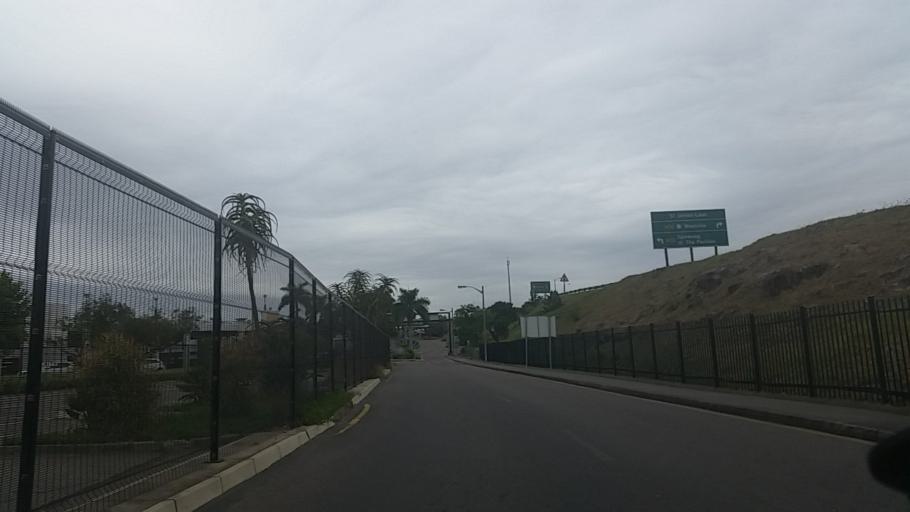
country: ZA
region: KwaZulu-Natal
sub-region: eThekwini Metropolitan Municipality
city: Berea
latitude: -29.8476
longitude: 30.9350
